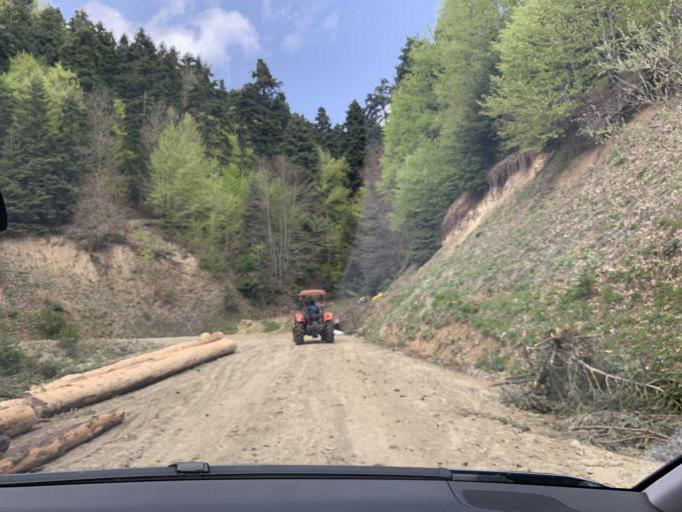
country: TR
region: Bolu
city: Bolu
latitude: 40.8396
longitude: 31.6683
